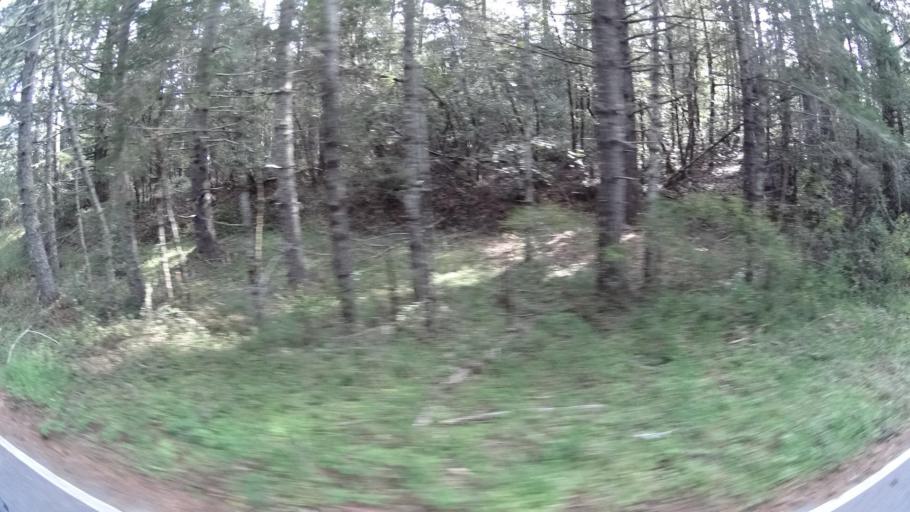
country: US
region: California
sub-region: Humboldt County
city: Blue Lake
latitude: 40.7431
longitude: -123.9622
